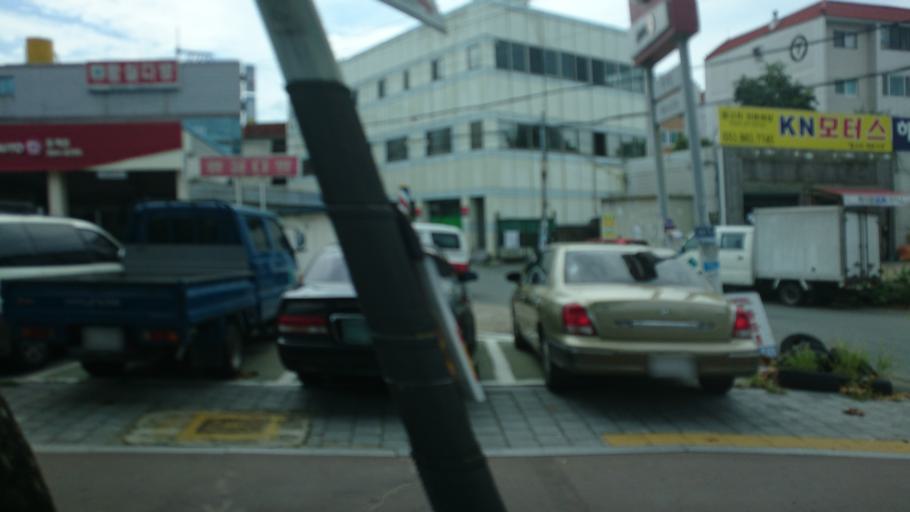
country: KR
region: Gyeongsangbuk-do
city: Gyeongsan-si
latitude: 35.8771
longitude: 128.6779
